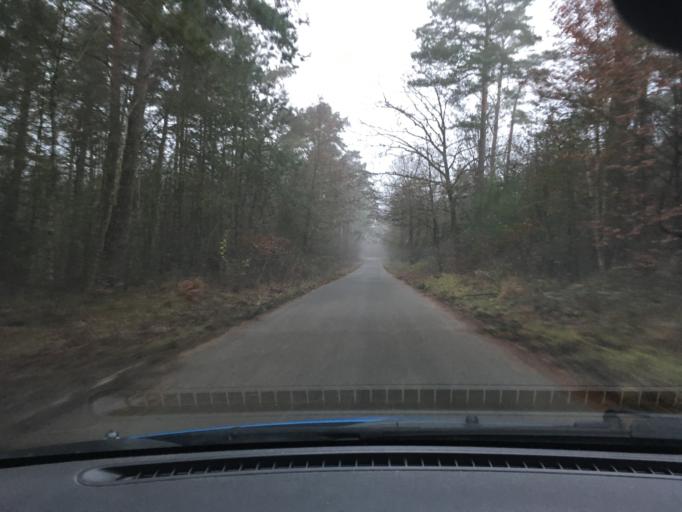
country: DE
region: Lower Saxony
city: Oldendorf
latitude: 53.1493
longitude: 10.1903
